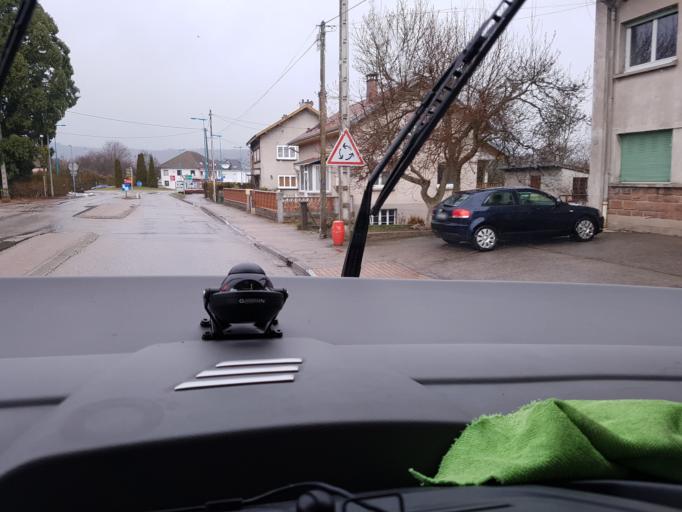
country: FR
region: Lorraine
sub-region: Departement des Vosges
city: Anould
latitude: 48.1878
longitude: 6.9546
